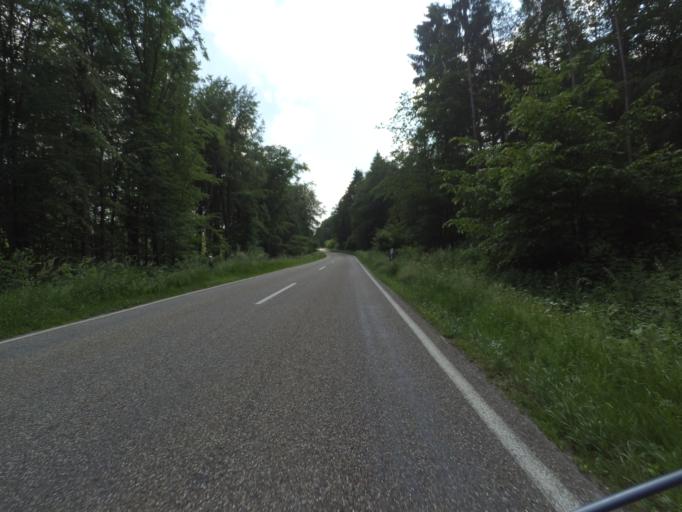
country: DE
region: Rheinland-Pfalz
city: Brohl
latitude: 50.2021
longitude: 7.2802
